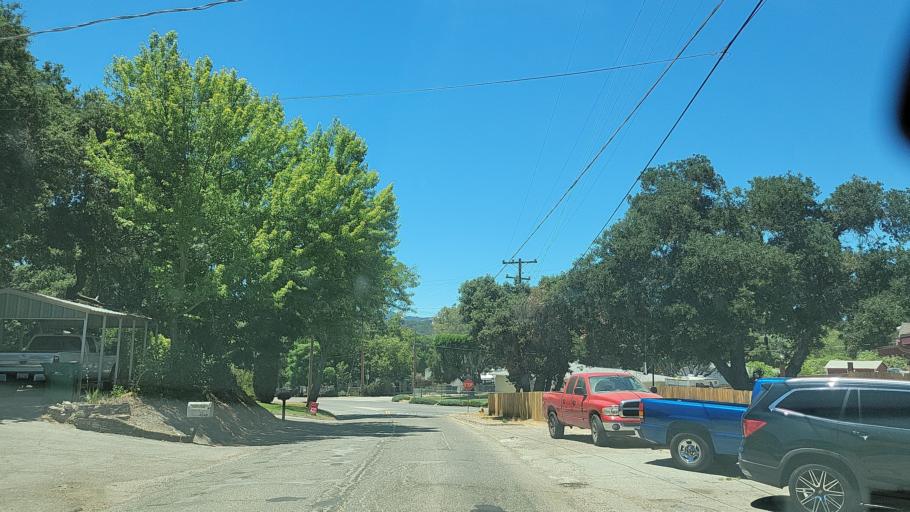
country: US
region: California
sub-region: San Luis Obispo County
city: Atascadero
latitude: 35.5054
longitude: -120.6805
